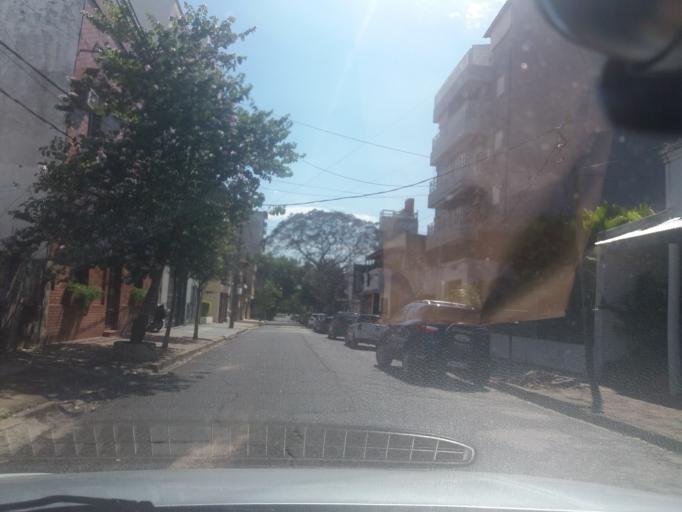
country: AR
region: Corrientes
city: Corrientes
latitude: -27.4678
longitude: -58.8455
